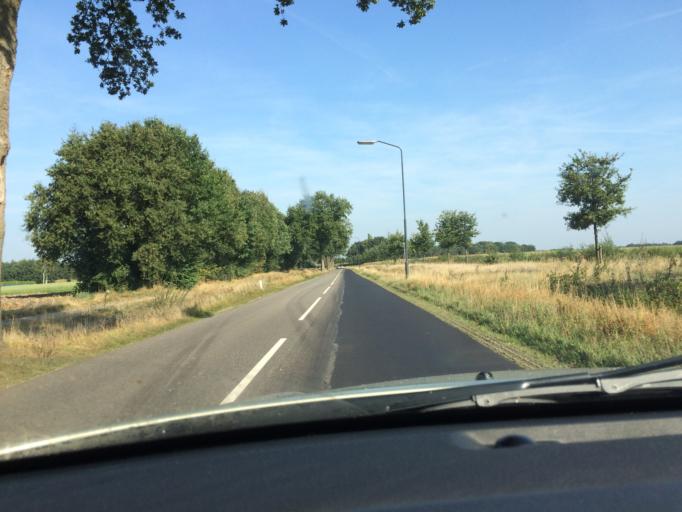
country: NL
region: North Brabant
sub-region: Gemeente Baarle-Nassau
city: Baarle-Nassau
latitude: 51.4537
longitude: 4.9430
